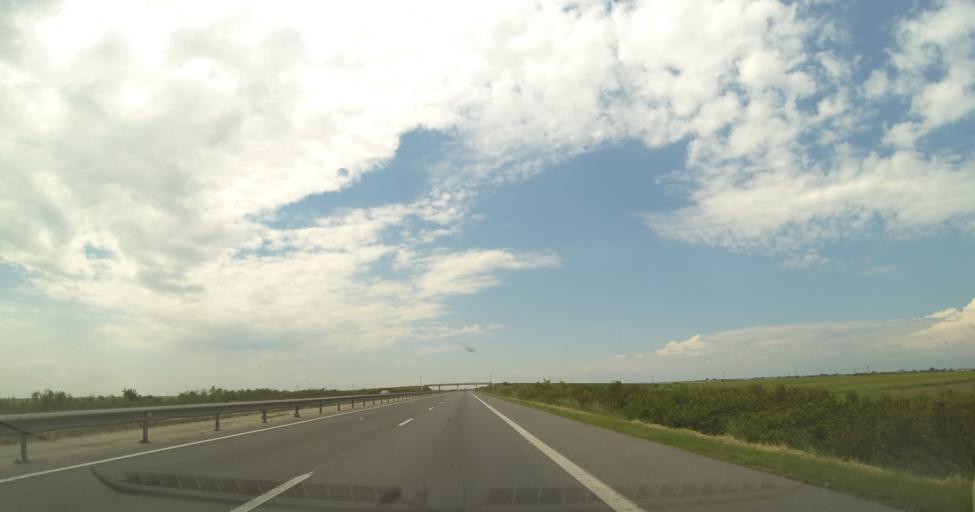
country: RO
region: Dambovita
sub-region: Comuna Petresti
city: Ionesti
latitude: 44.6715
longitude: 25.2976
